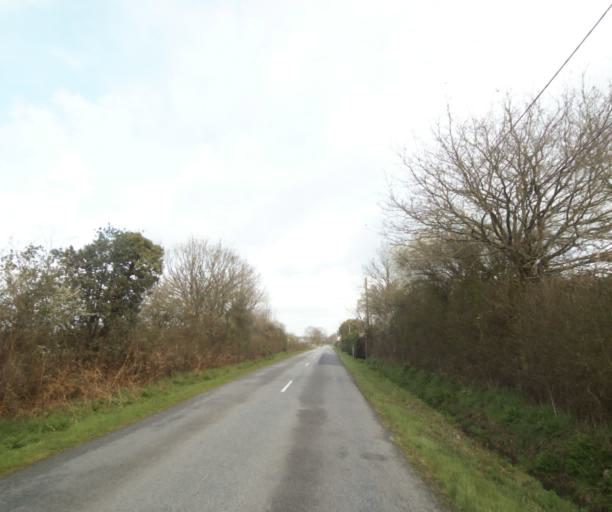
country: FR
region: Pays de la Loire
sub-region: Departement de la Loire-Atlantique
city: Bouvron
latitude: 47.4065
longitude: -1.8873
